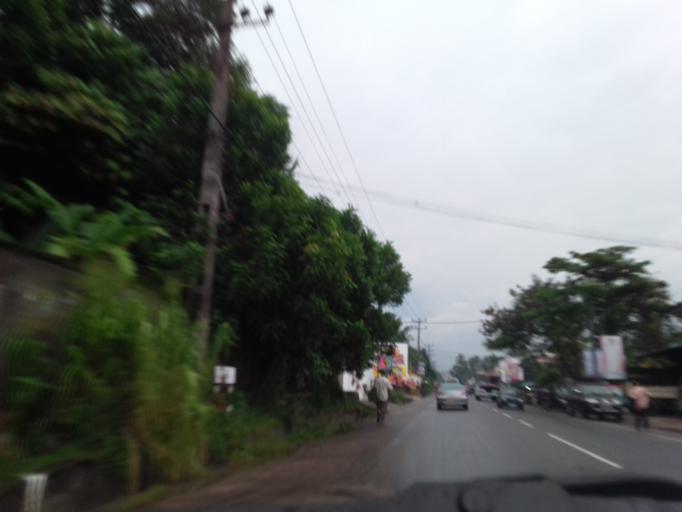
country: LK
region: Western
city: Battaramulla South
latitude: 6.8927
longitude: 79.9630
